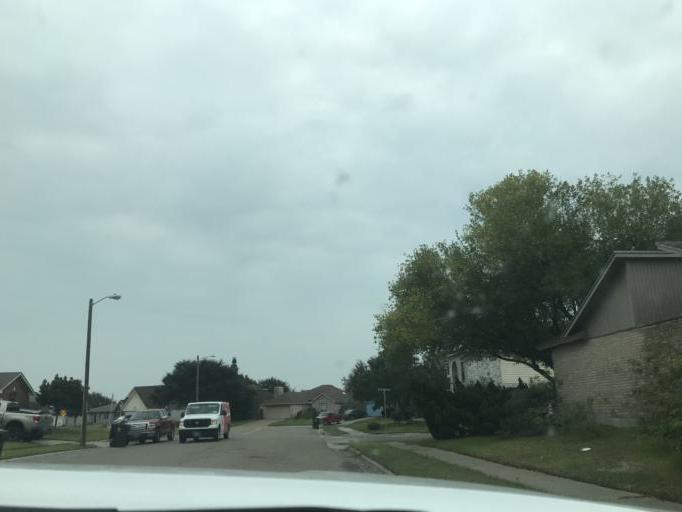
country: US
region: Texas
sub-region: Nueces County
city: Corpus Christi
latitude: 27.6684
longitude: -97.3525
